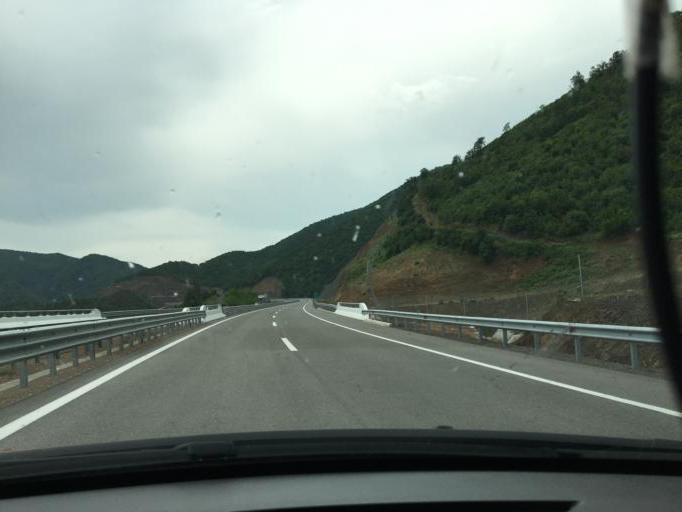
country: MK
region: Gevgelija
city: Miravci
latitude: 41.3580
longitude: 22.3536
